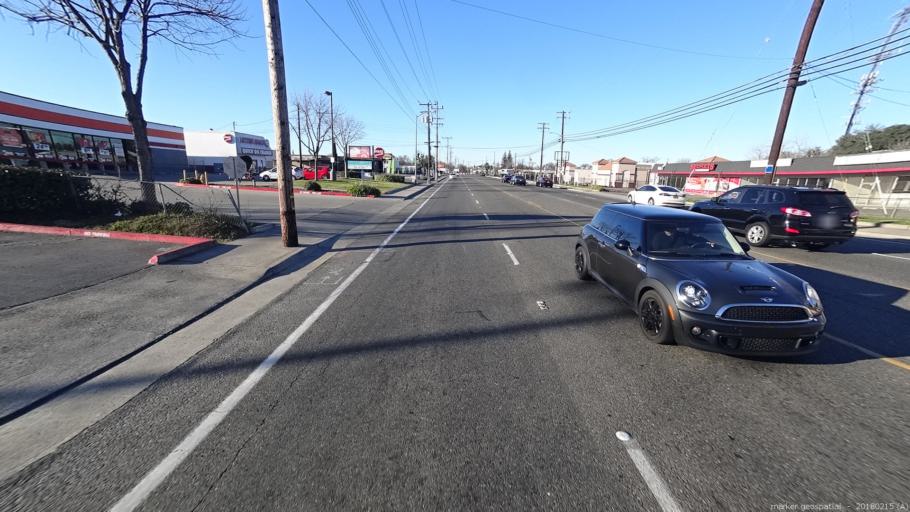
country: US
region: California
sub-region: Sacramento County
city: Foothill Farms
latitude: 38.6723
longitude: -121.3291
